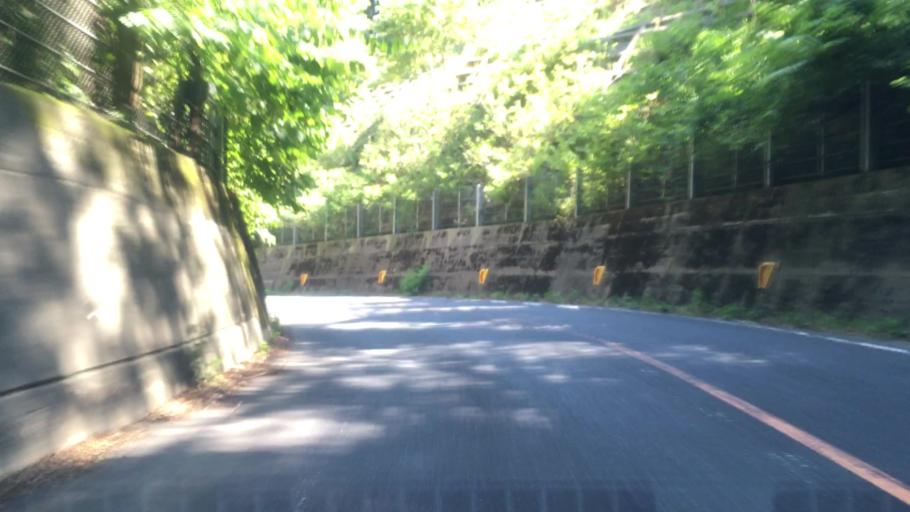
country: JP
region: Hyogo
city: Toyooka
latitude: 35.5931
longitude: 134.9136
